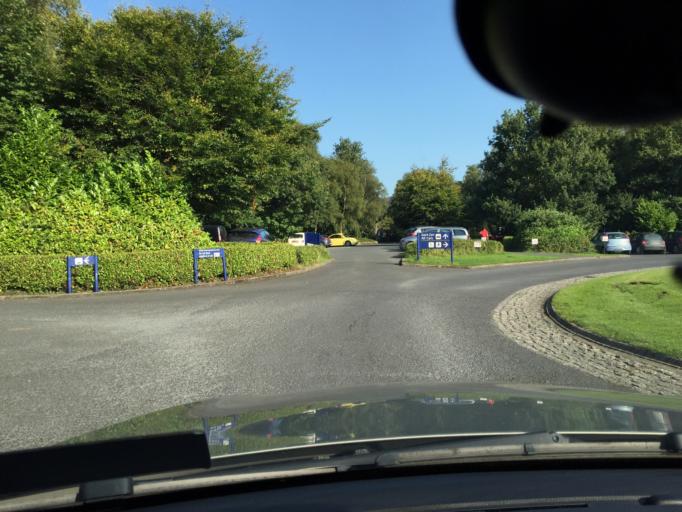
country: IE
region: Leinster
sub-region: Wicklow
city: Rathdrum
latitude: 53.0106
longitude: -6.3235
